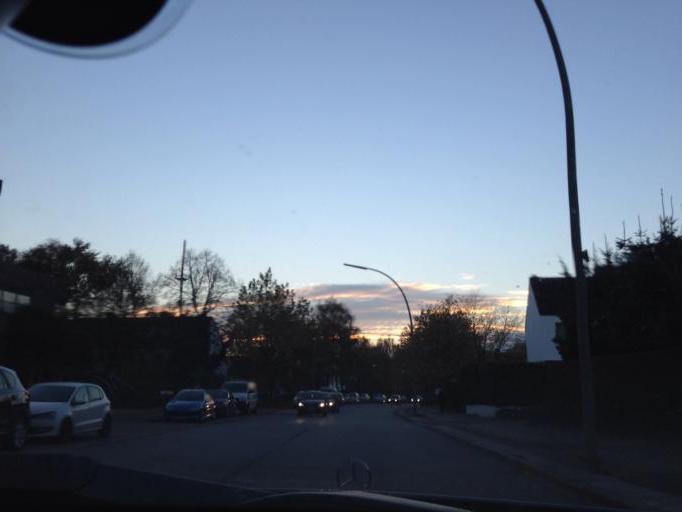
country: DE
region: Hamburg
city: Wandsbek
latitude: 53.5762
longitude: 10.0993
